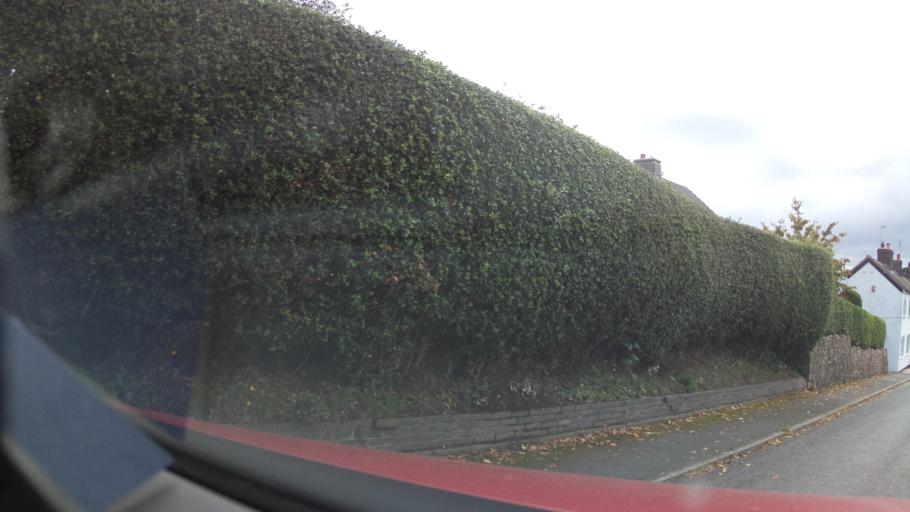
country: GB
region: England
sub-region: Staffordshire
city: Barlaston
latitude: 52.9462
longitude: -2.1580
